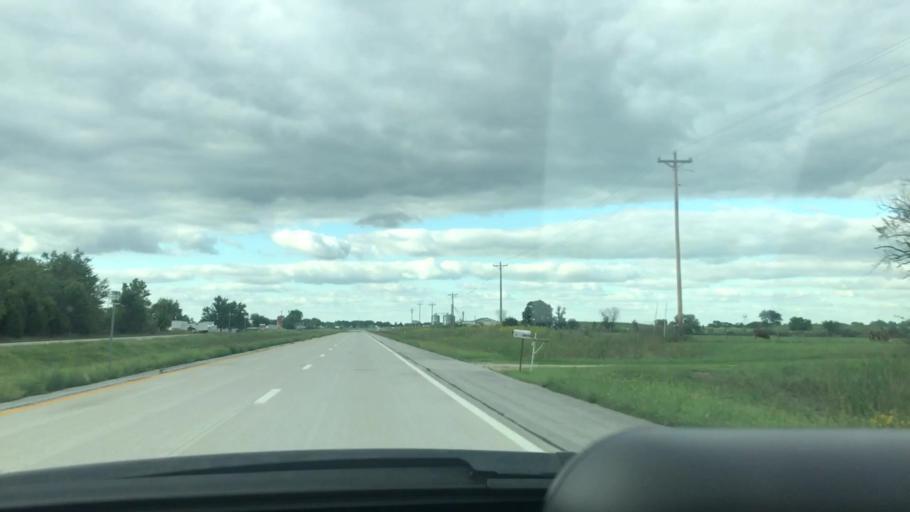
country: US
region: Missouri
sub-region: Benton County
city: Lincoln
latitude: 38.3693
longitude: -93.3387
